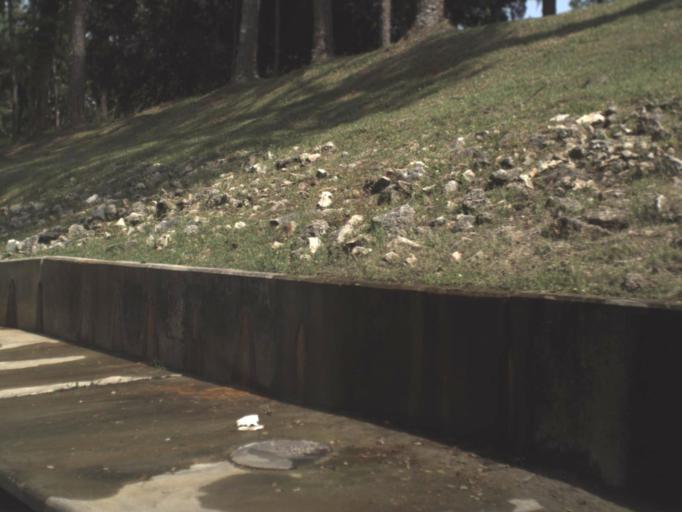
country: US
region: Florida
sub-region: Putnam County
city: Palatka
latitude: 29.6436
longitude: -81.6420
